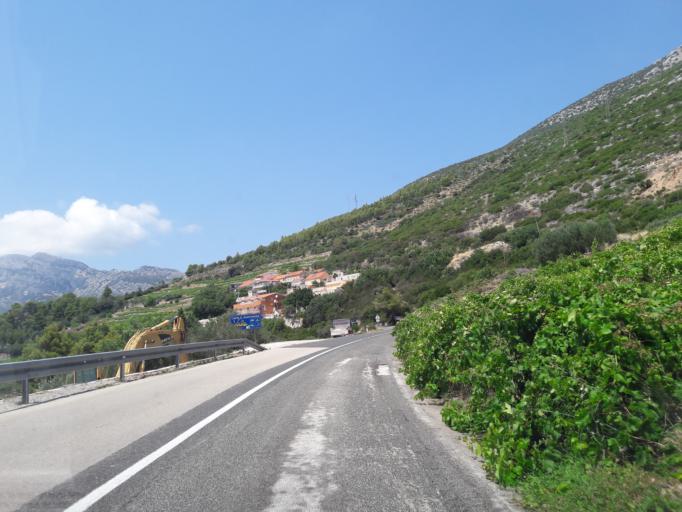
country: HR
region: Dubrovacko-Neretvanska
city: Orebic
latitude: 42.9775
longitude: 17.2280
